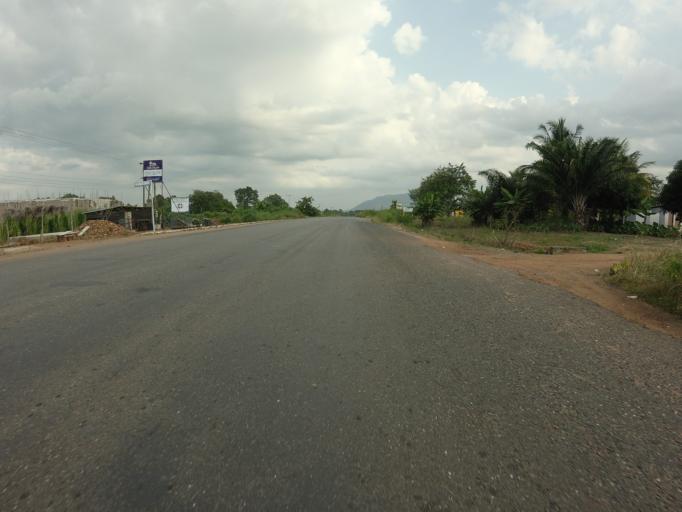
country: GH
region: Volta
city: Ho
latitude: 6.5757
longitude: 0.4836
